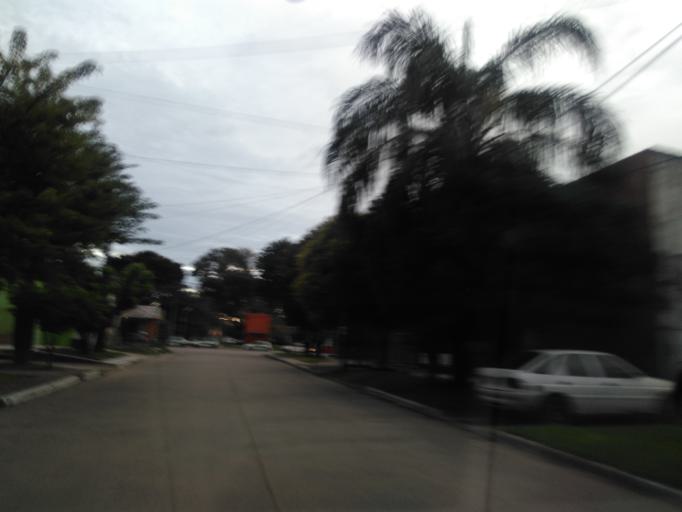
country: AR
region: Chaco
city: Resistencia
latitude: -27.4429
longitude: -58.9762
